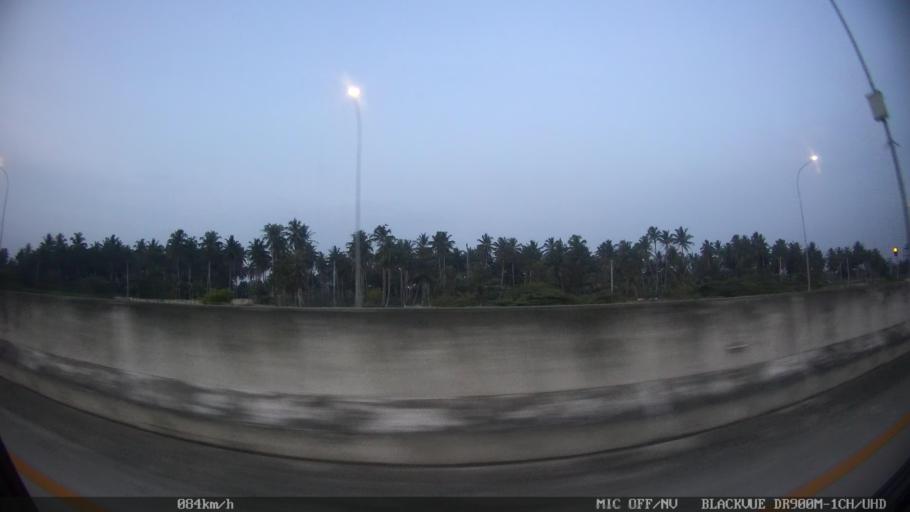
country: ID
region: Lampung
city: Kalianda
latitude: -5.6508
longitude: 105.5827
